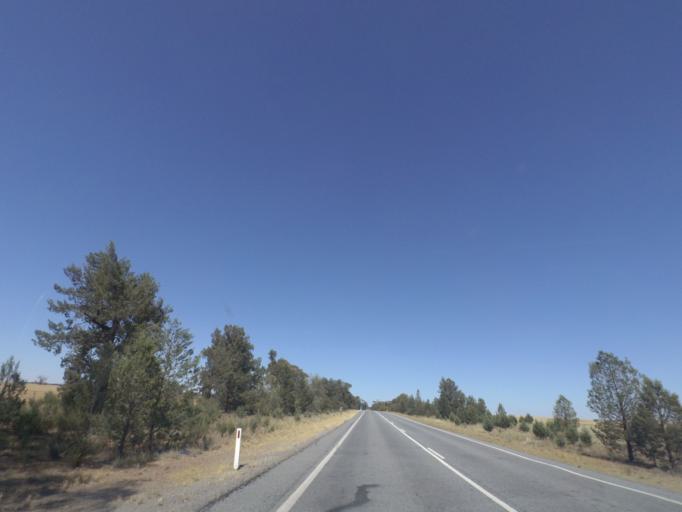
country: AU
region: New South Wales
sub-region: Narrandera
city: Narrandera
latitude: -34.4137
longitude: 146.8671
